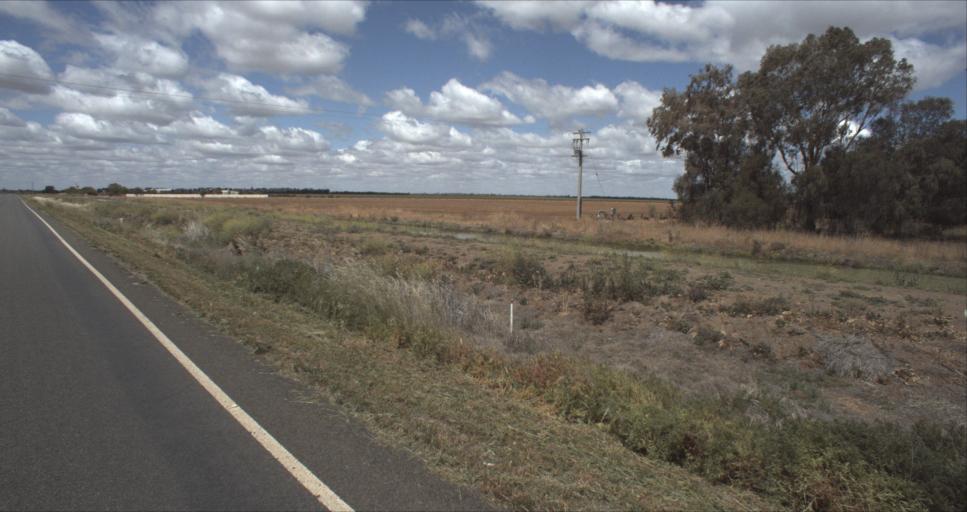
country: AU
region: New South Wales
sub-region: Murrumbidgee Shire
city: Darlington Point
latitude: -34.4835
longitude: 146.1570
